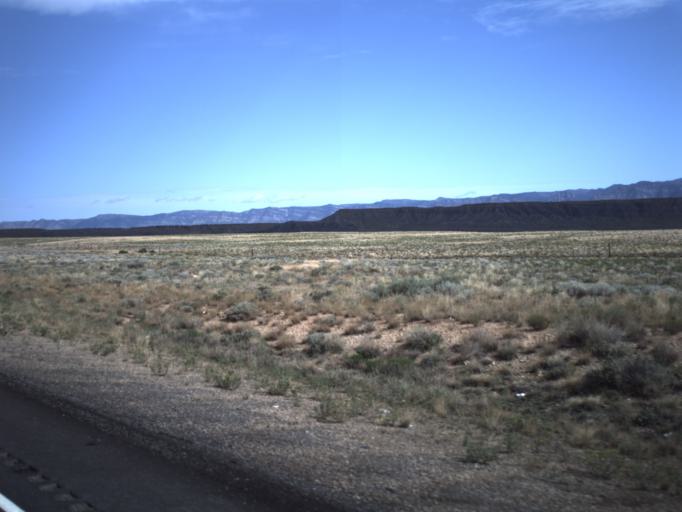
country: US
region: Utah
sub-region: Carbon County
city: East Carbon City
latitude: 39.4796
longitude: -110.5088
